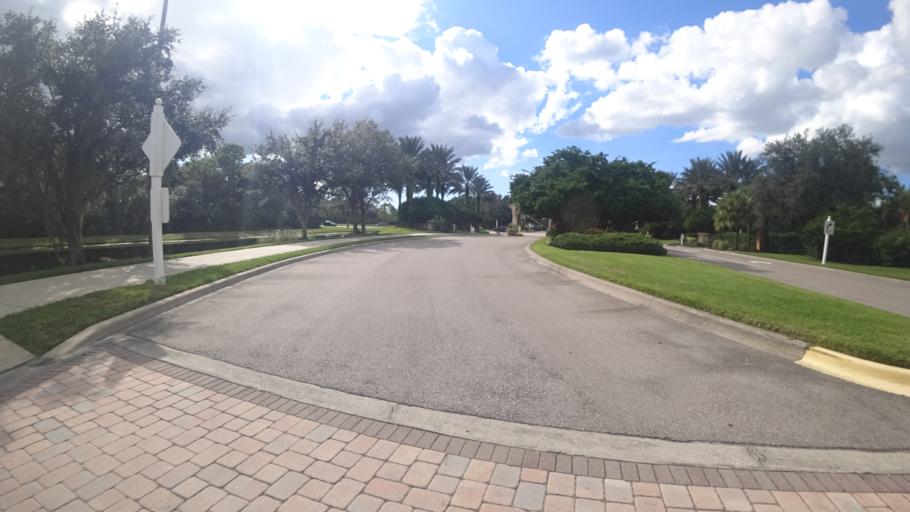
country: US
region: Florida
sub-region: Sarasota County
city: The Meadows
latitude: 27.4070
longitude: -82.4276
